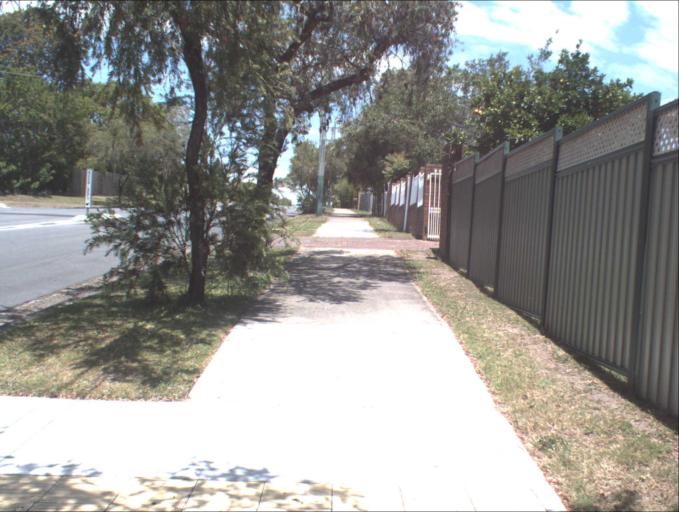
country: AU
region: Queensland
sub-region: Logan
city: Rochedale South
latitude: -27.5898
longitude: 153.1384
